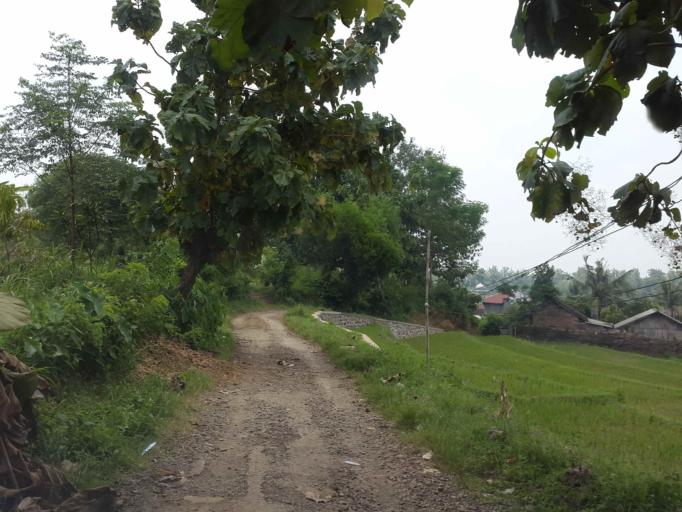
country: ID
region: Central Java
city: Pamedaran
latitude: -7.0698
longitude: 108.8621
